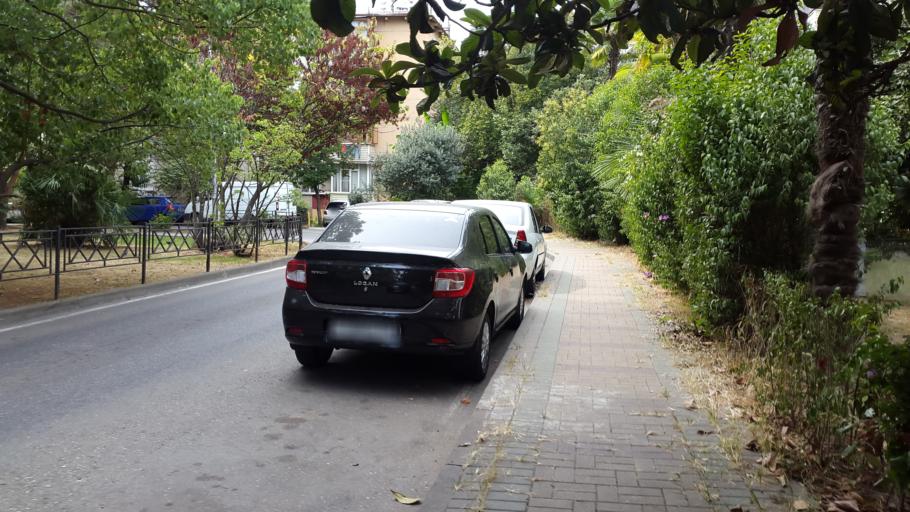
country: RU
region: Krasnodarskiy
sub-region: Sochi City
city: Sochi
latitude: 43.6025
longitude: 39.7251
